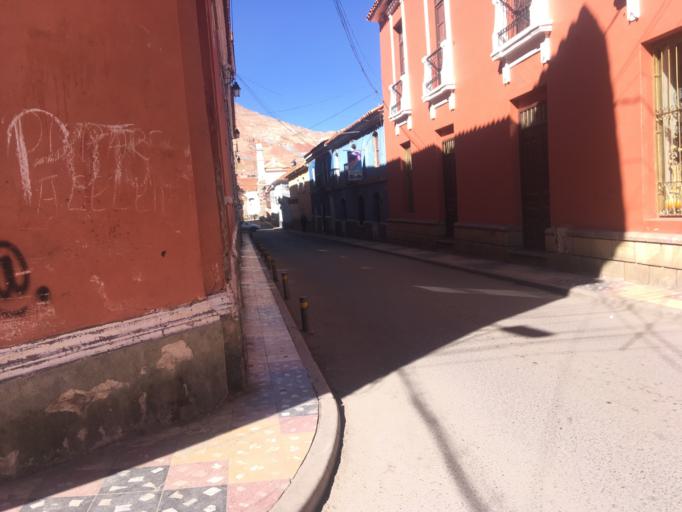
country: BO
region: Potosi
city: Potosi
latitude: -19.5884
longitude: -65.7555
